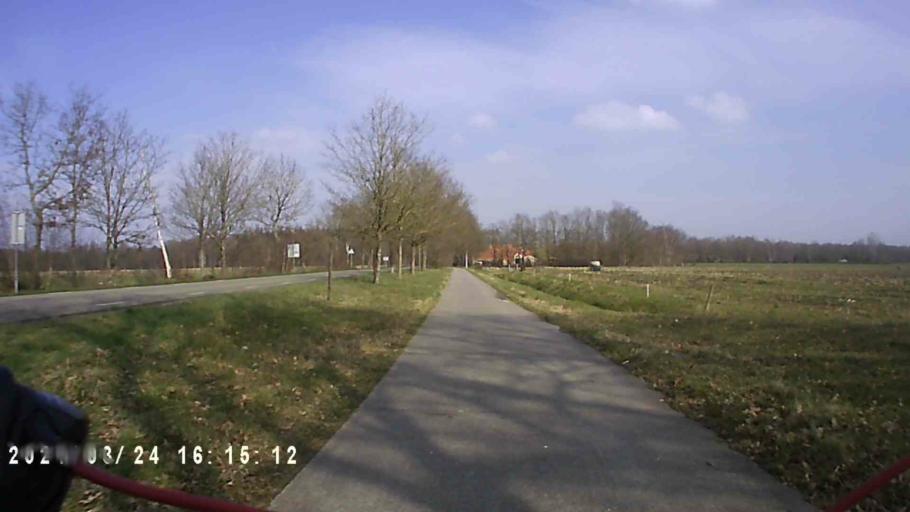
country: NL
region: Friesland
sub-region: Gemeente Heerenveen
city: Jubbega
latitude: 53.0435
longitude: 6.2363
